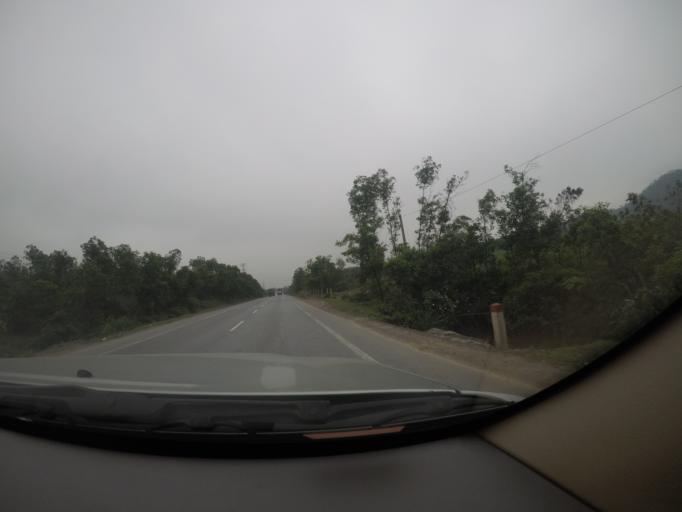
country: VN
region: Ha Tinh
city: Ky Anh
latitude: 18.0281
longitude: 106.3373
